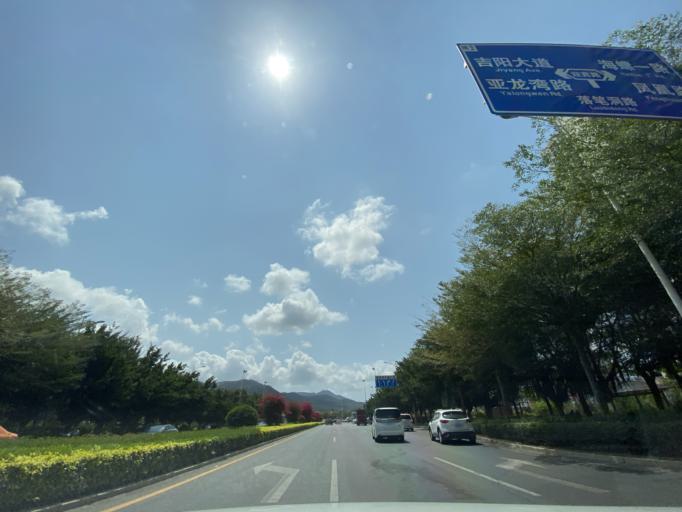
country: CN
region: Hainan
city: Tiandu
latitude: 18.2942
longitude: 109.5289
